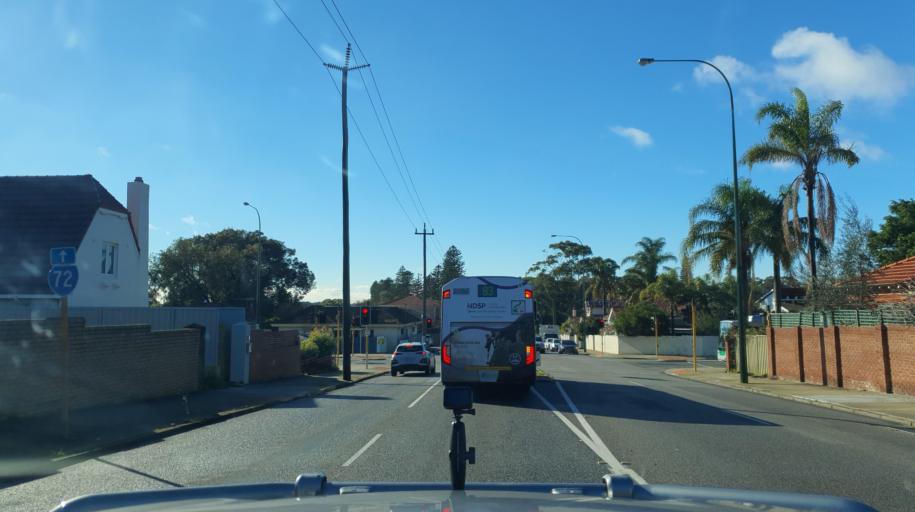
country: AU
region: Western Australia
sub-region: Cambridge
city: West Leederville
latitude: -31.9343
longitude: 115.8194
